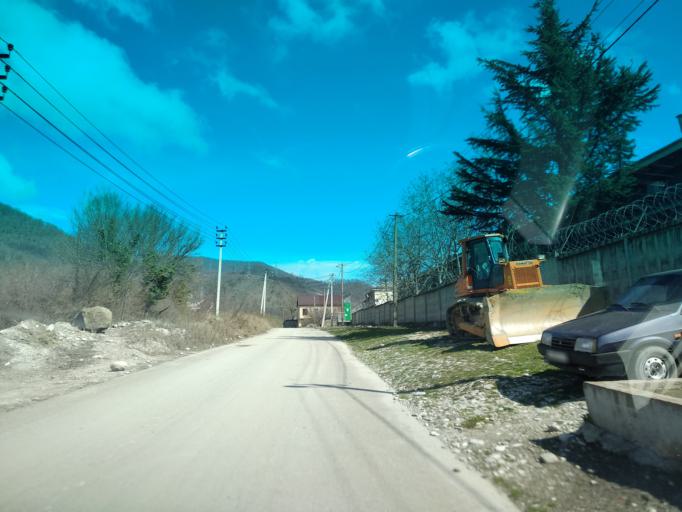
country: RU
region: Krasnodarskiy
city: Shepsi
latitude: 44.0548
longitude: 39.1639
